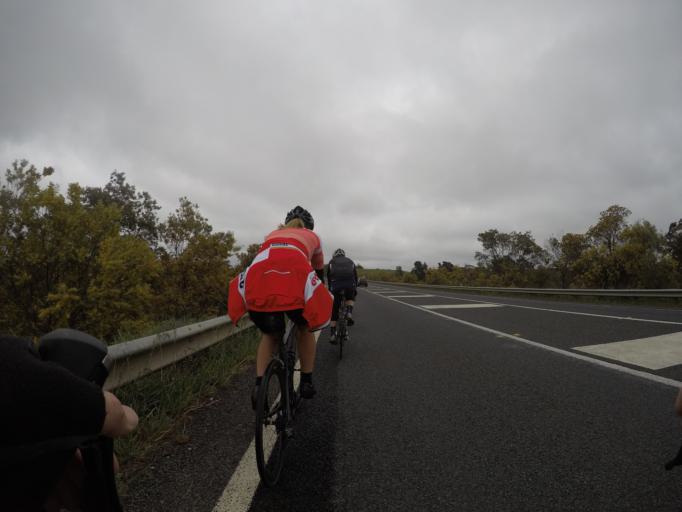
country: AU
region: New South Wales
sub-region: Lithgow
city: Portland
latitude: -33.4525
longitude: 149.9680
